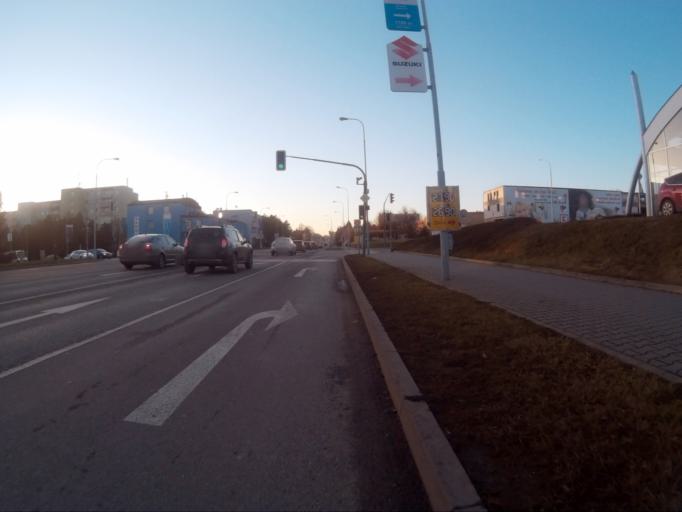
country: CZ
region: South Moravian
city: Moravany
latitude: 49.1734
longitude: 16.5845
